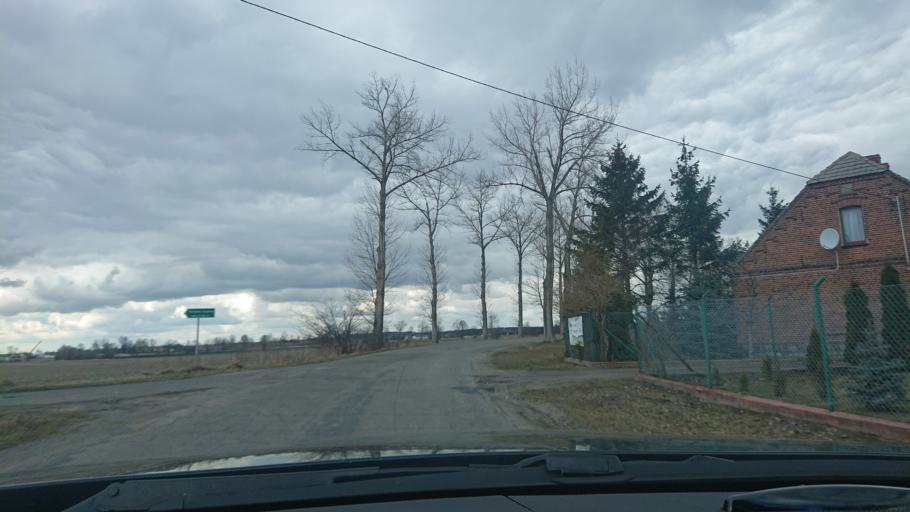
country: PL
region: Greater Poland Voivodeship
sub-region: Powiat gnieznienski
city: Niechanowo
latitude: 52.5846
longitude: 17.7018
